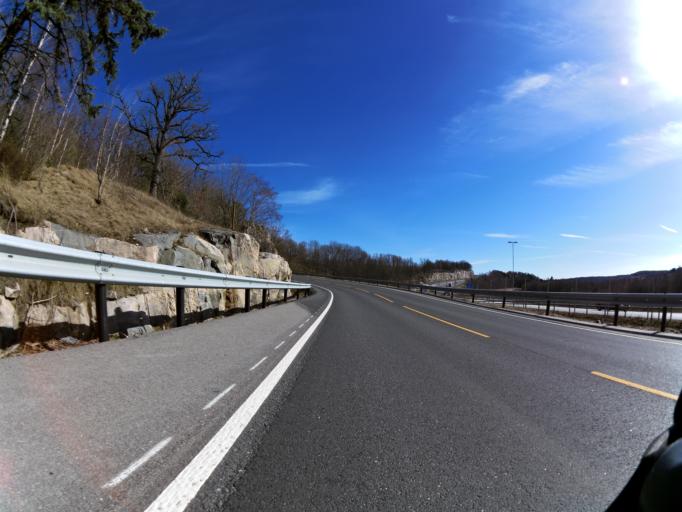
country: NO
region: Ostfold
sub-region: Rade
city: Karlshus
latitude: 59.3248
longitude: 10.9623
